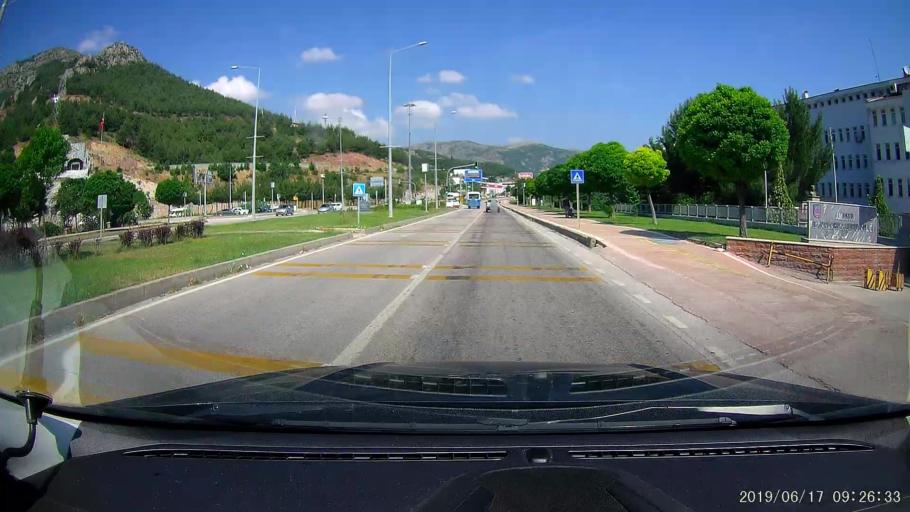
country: TR
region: Amasya
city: Amasya
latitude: 40.6699
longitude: 35.8347
